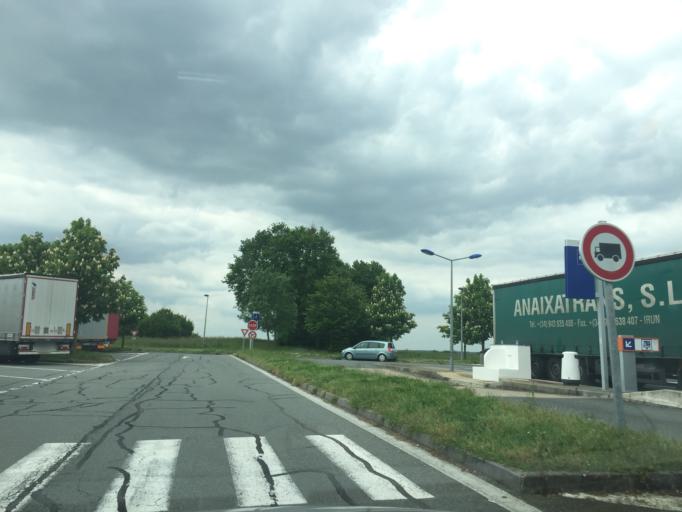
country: FR
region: Poitou-Charentes
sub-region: Departement des Deux-Sevres
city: Saint-Maxire
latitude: 46.4304
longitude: -0.5039
